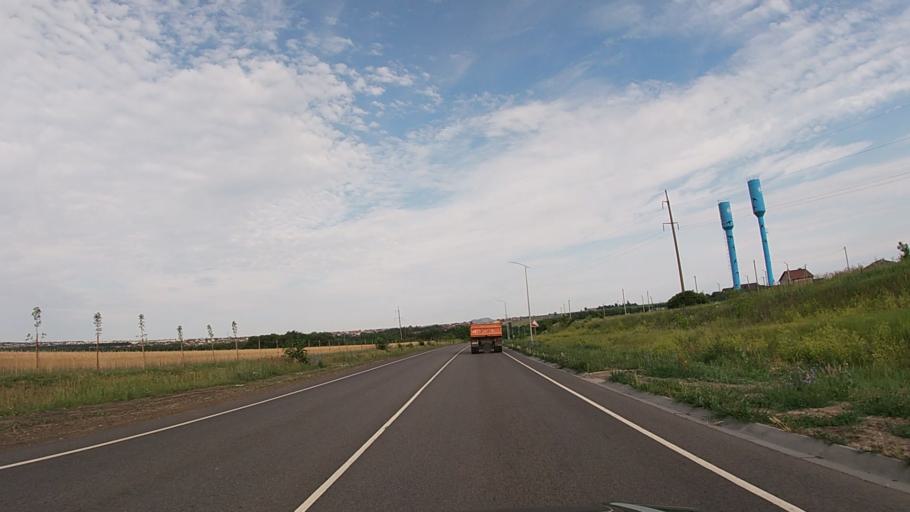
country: RU
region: Belgorod
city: Severnyy
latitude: 50.6658
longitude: 36.4981
